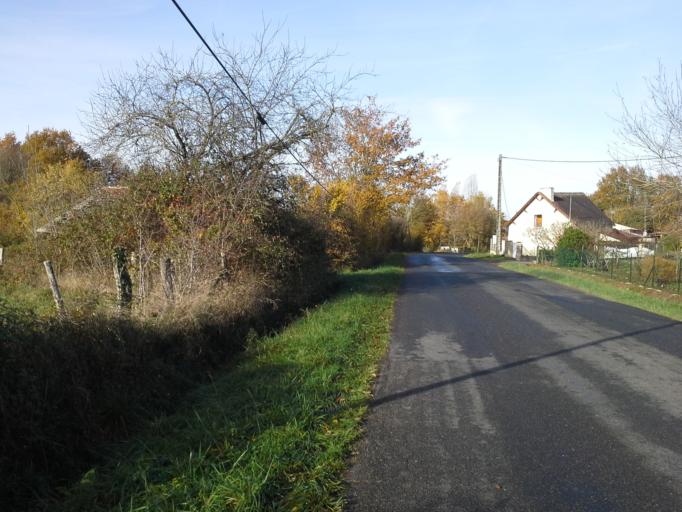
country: FR
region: Poitou-Charentes
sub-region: Departement de la Vienne
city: Pleumartin
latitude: 46.6350
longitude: 0.7546
